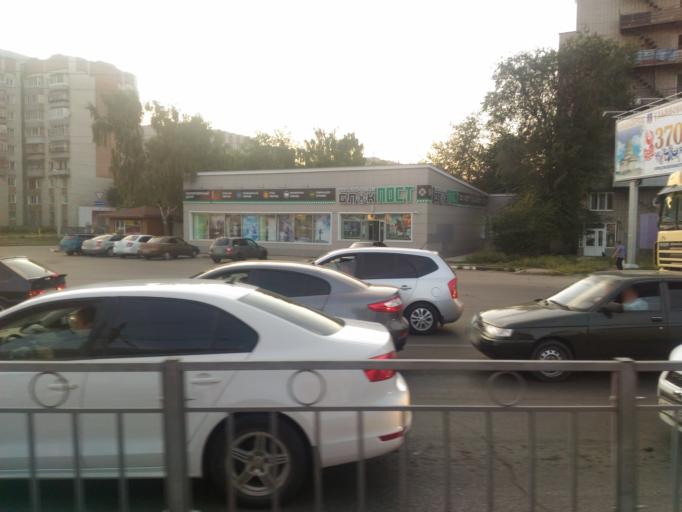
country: RU
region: Ulyanovsk
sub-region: Ulyanovskiy Rayon
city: Ulyanovsk
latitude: 54.2862
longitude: 48.3027
